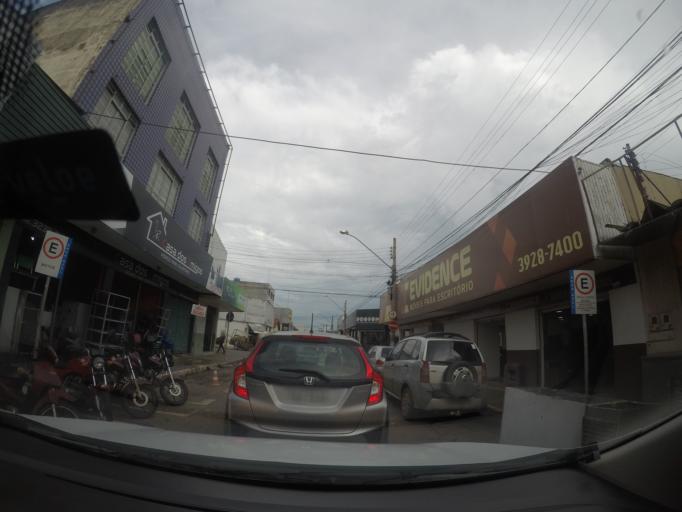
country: BR
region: Goias
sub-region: Goiania
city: Goiania
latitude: -16.6717
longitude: -49.2866
